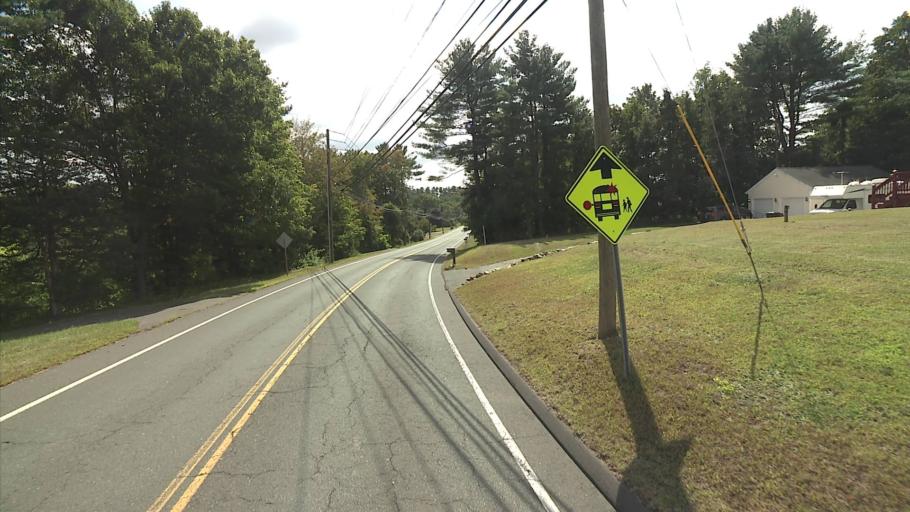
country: US
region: Connecticut
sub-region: Hartford County
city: Salmon Brook
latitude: 41.9683
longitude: -72.8042
